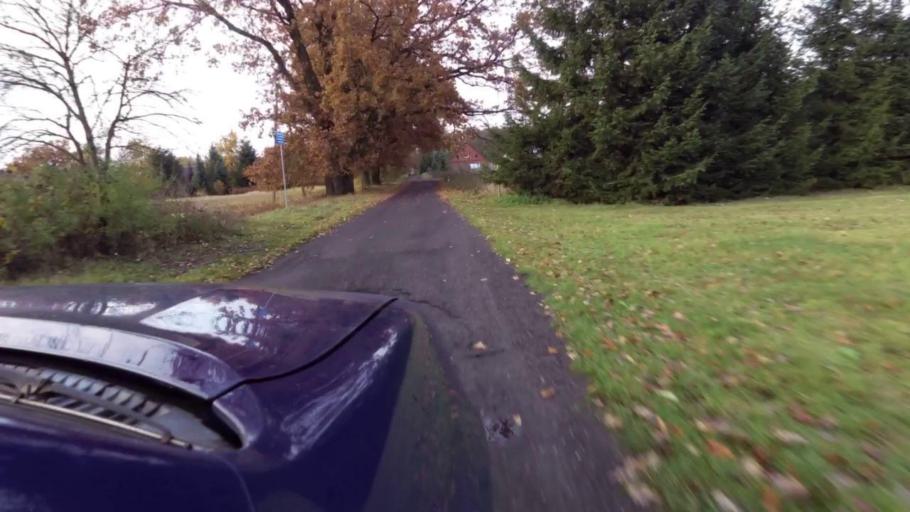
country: PL
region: West Pomeranian Voivodeship
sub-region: Powiat goleniowski
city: Goleniow
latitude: 53.6062
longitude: 14.7540
